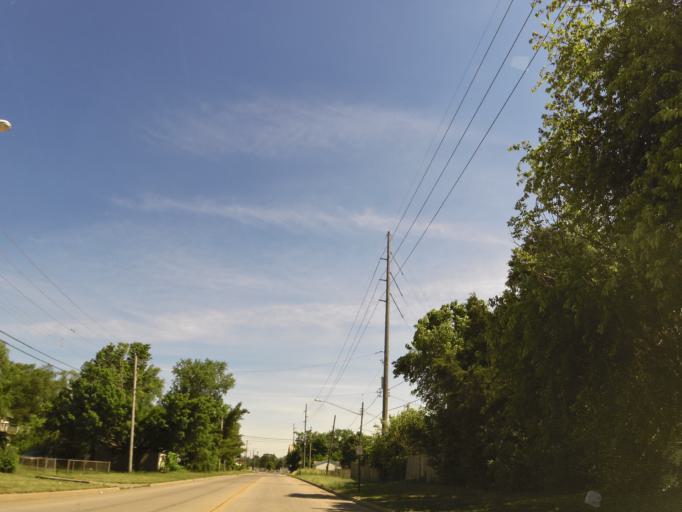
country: US
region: Illinois
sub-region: Vermilion County
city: Danville
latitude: 40.1326
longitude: -87.5865
